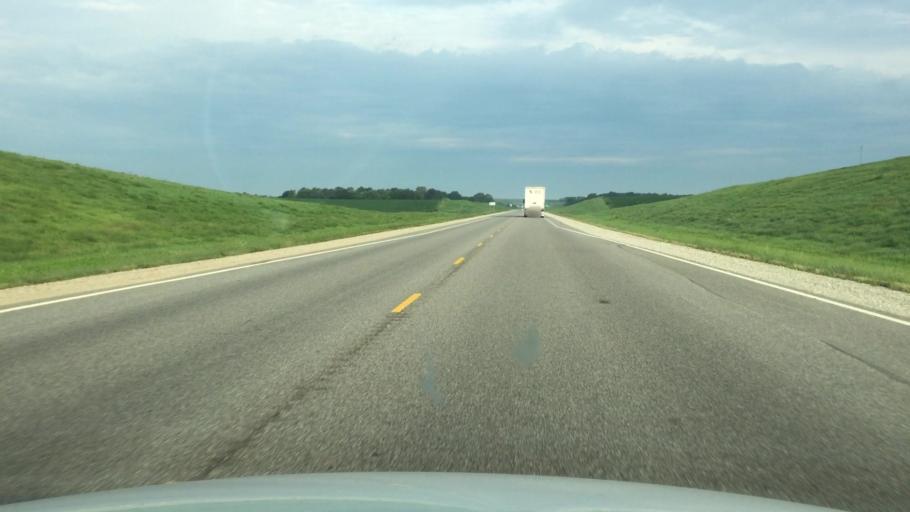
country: US
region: Kansas
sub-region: Doniphan County
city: Highland
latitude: 39.8366
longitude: -95.2469
